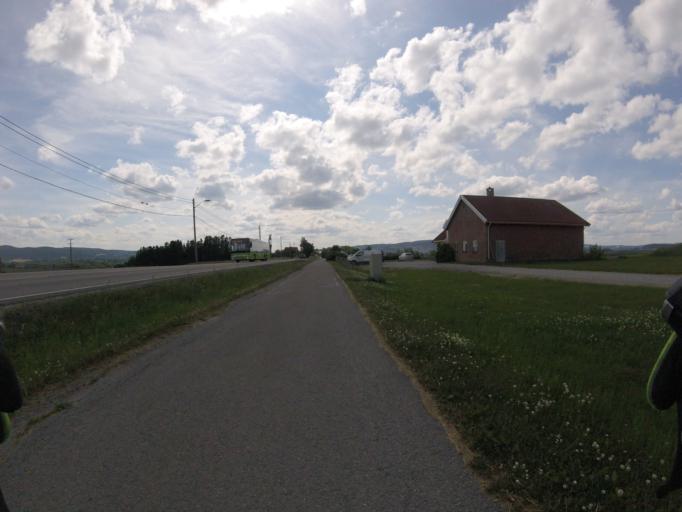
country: NO
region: Akershus
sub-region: Skedsmo
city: Lillestrom
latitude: 59.9792
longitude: 11.0553
